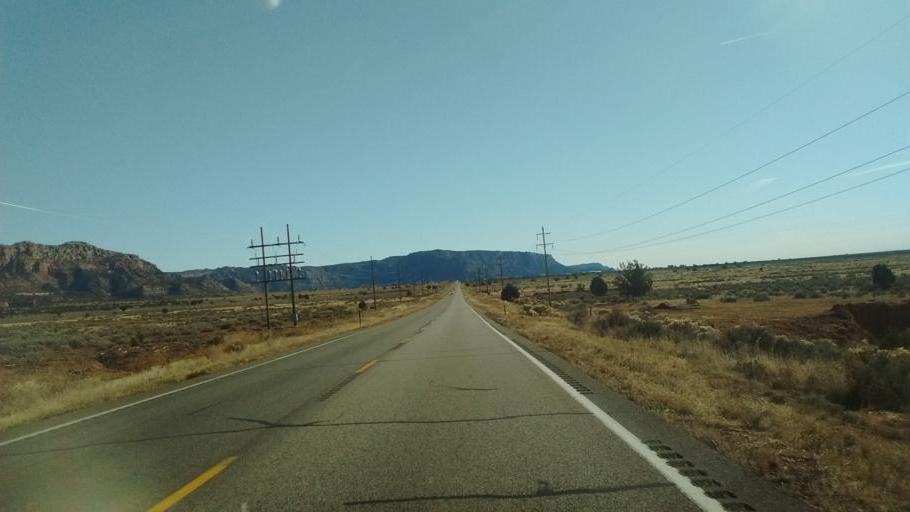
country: US
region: Arizona
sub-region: Mohave County
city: Colorado City
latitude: 37.0187
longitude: -113.0323
